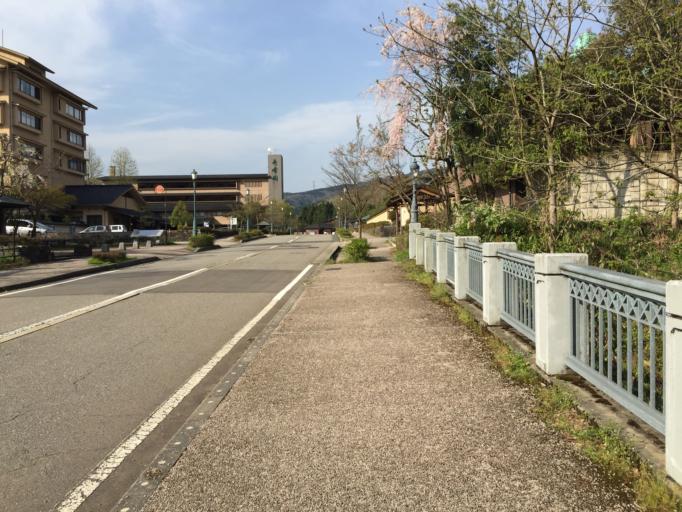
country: JP
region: Ishikawa
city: Tsurugi-asahimachi
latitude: 36.4887
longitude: 136.7557
